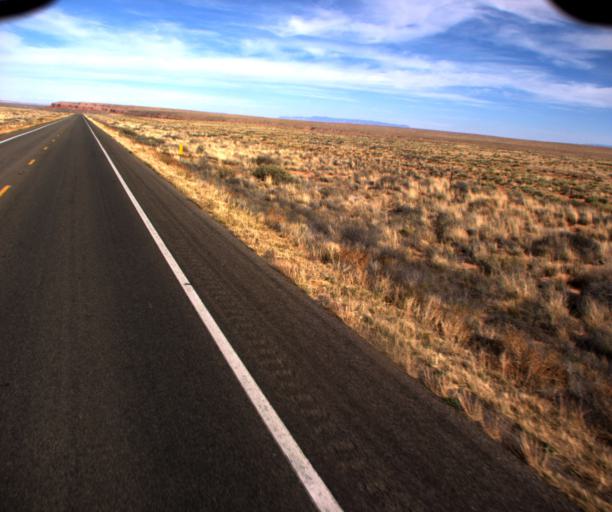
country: US
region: Arizona
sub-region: Navajo County
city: Kayenta
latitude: 36.7361
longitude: -110.0910
